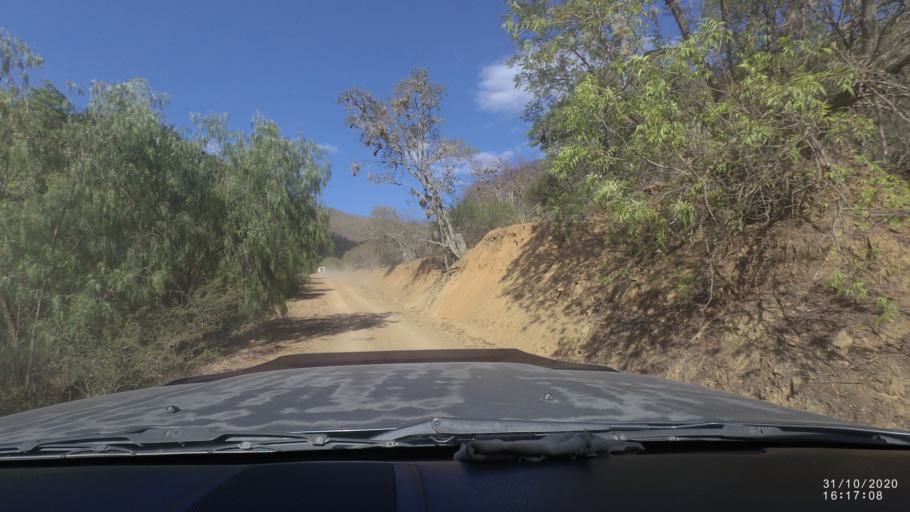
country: BO
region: Chuquisaca
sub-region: Provincia Zudanez
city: Mojocoya
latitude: -18.3907
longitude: -64.6053
